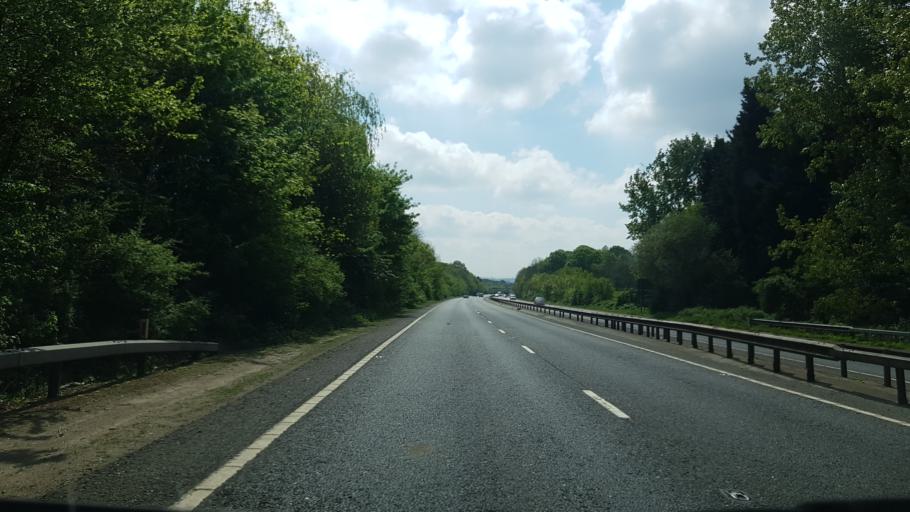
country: GB
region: England
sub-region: Kent
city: Sevenoaks
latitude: 51.2326
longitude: 0.2159
